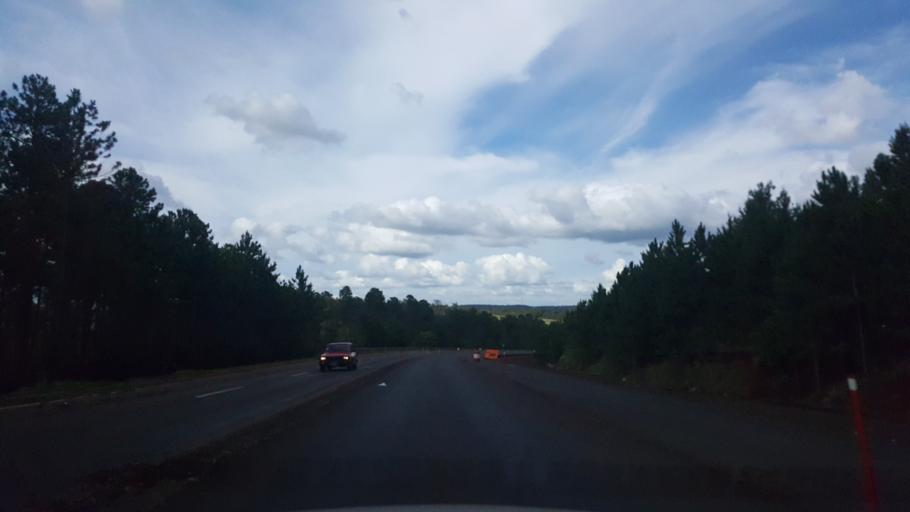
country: AR
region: Misiones
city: Santa Ana
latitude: -27.3923
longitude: -55.5988
